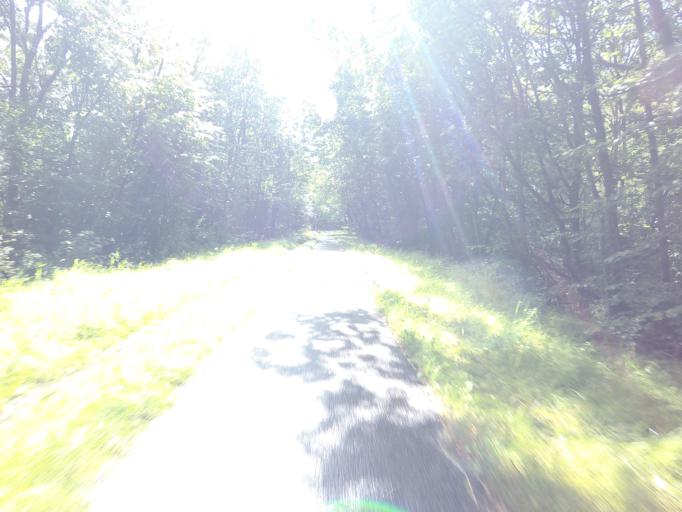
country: DK
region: Central Jutland
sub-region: Silkeborg Kommune
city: Silkeborg
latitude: 56.1167
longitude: 9.4198
